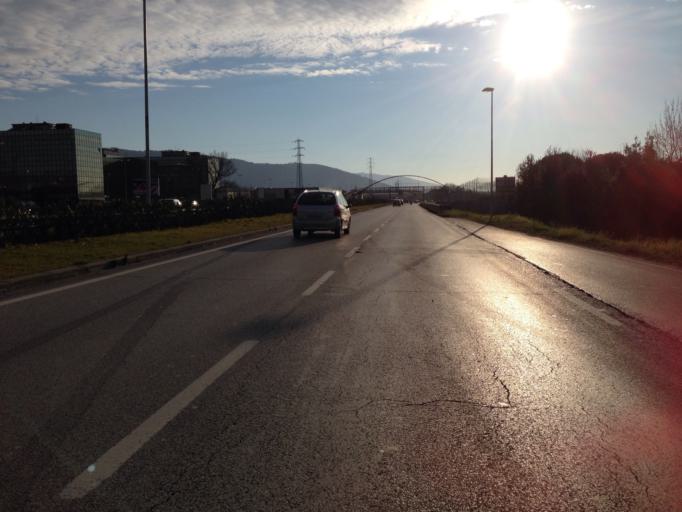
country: IT
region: Tuscany
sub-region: Provincia di Prato
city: Prato
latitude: 43.8778
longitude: 11.0686
